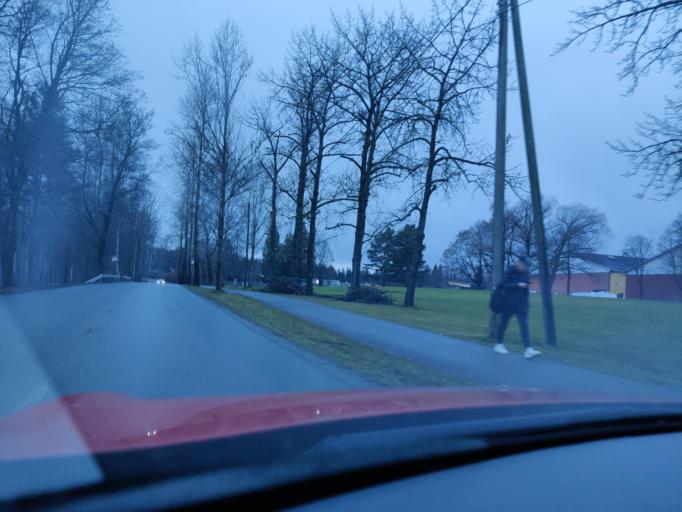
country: FI
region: Pirkanmaa
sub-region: Tampere
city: Nokia
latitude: 61.4832
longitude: 23.5300
